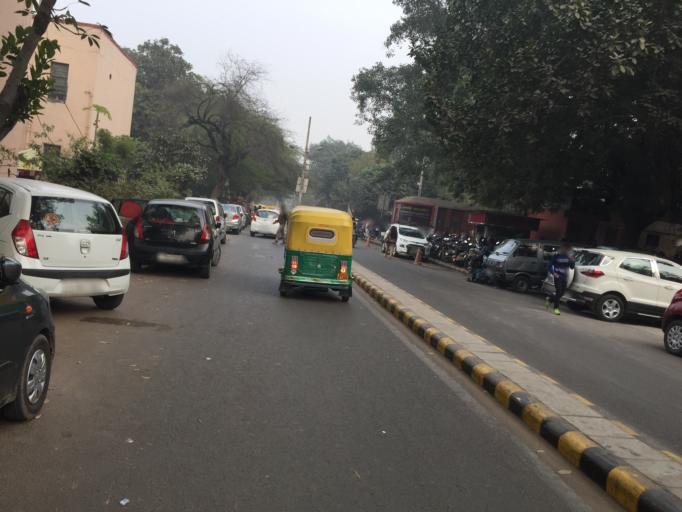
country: IN
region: NCT
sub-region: New Delhi
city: New Delhi
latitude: 28.5782
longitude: 77.1966
